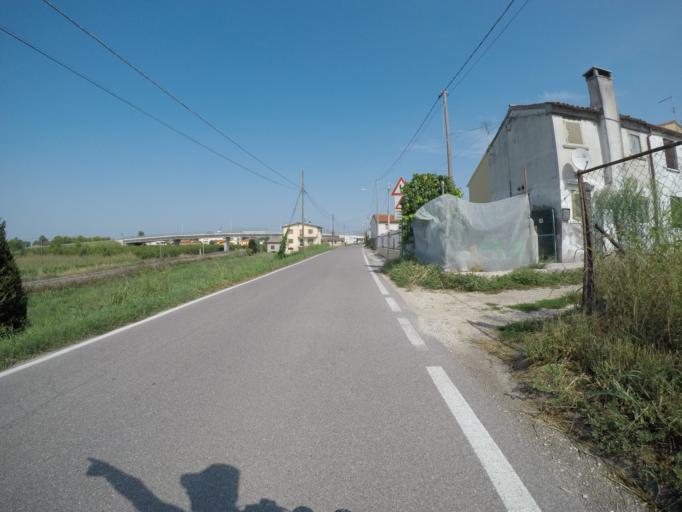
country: IT
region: Veneto
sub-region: Provincia di Rovigo
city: Lendinara
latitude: 45.0736
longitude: 11.6038
